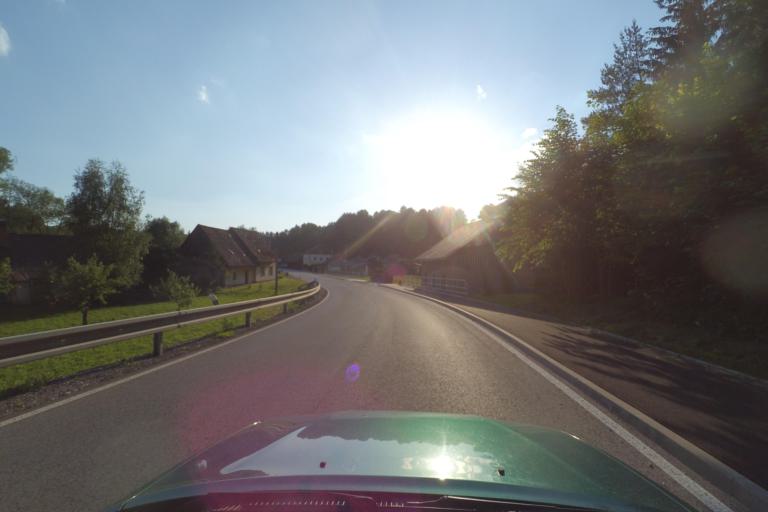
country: CZ
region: Kralovehradecky
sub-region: Okres Trutnov
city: Rudnik
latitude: 50.5775
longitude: 15.7326
